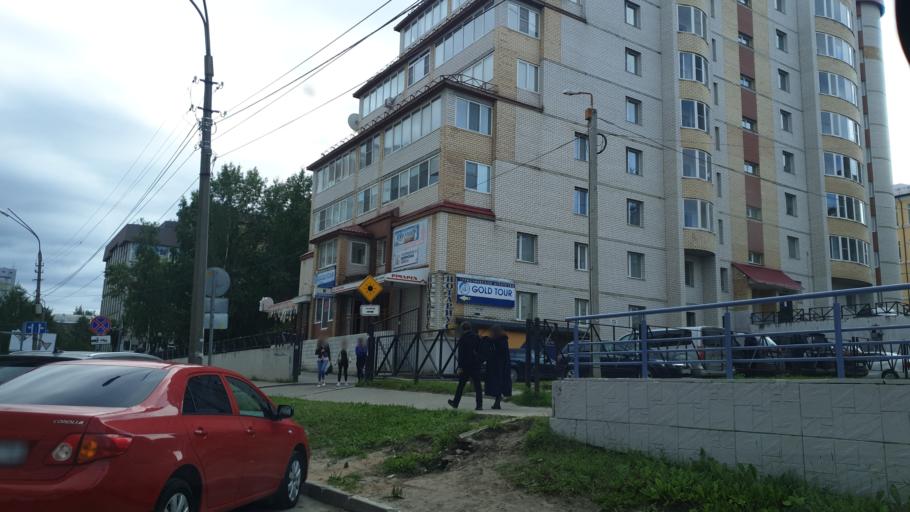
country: RU
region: Komi Republic
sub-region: Syktyvdinskiy Rayon
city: Syktyvkar
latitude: 61.6731
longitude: 50.8248
